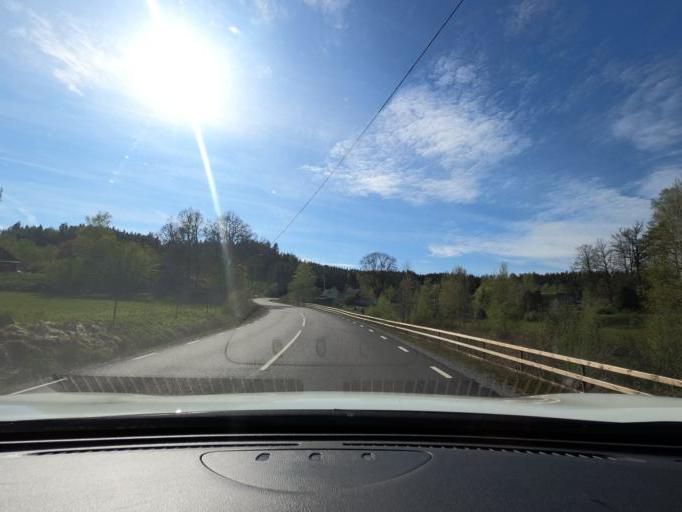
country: SE
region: Vaestra Goetaland
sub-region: Harryda Kommun
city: Landvetter
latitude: 57.6166
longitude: 12.2857
